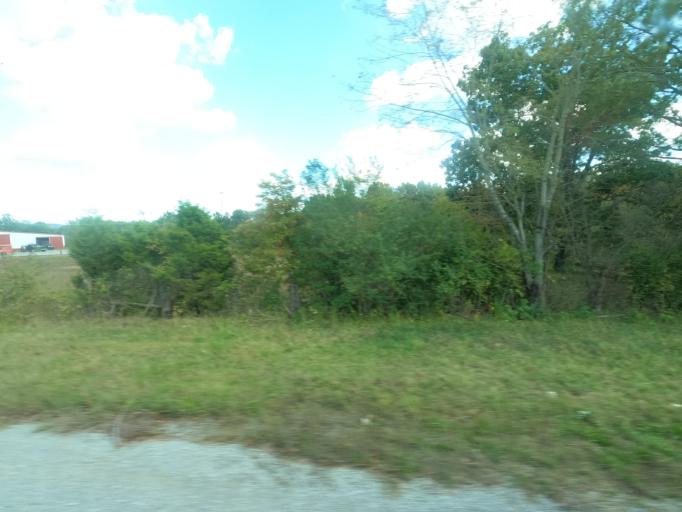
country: US
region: Illinois
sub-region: Johnson County
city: Vienna
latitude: 37.4326
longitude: -88.8928
